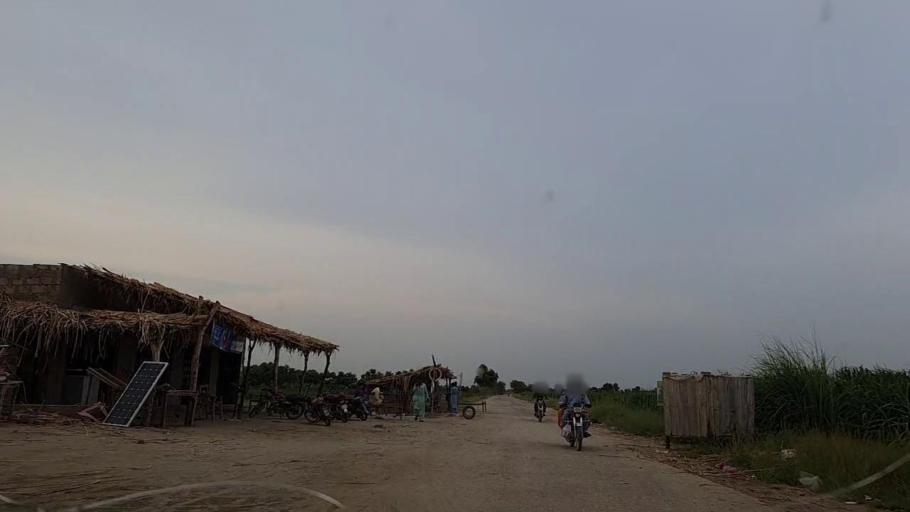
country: PK
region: Sindh
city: Mirpur Mathelo
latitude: 27.8803
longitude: 69.6376
